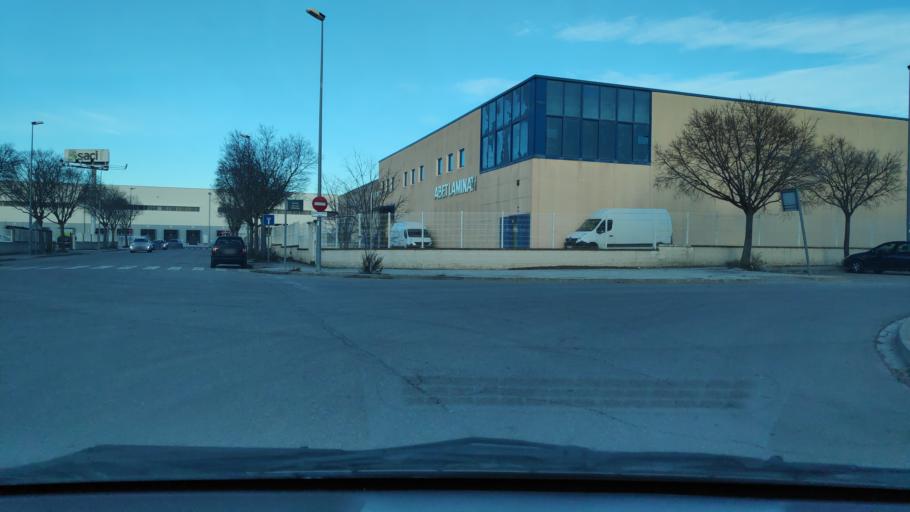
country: ES
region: Catalonia
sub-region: Provincia de Barcelona
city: Llica de Vall
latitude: 41.5714
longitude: 2.2682
